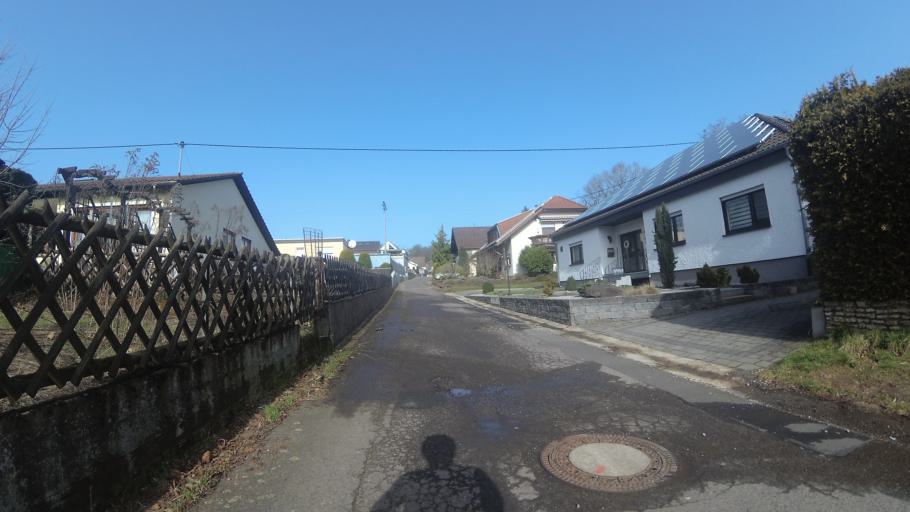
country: DE
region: Saarland
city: Uberherrn
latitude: 49.2730
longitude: 6.7020
